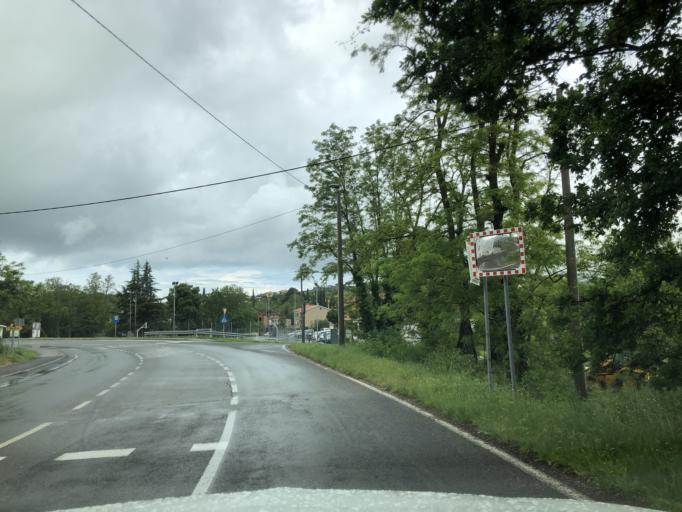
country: SI
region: Koper-Capodistria
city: Prade
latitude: 45.5174
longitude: 13.7794
